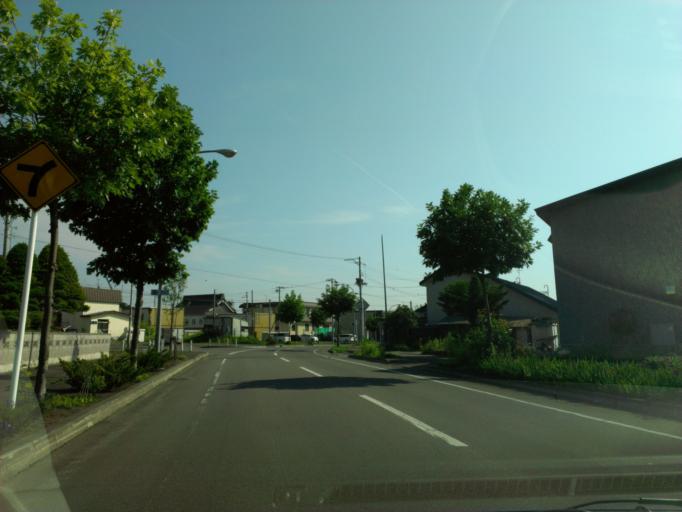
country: JP
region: Hokkaido
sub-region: Asahikawa-shi
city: Asahikawa
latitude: 43.5957
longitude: 142.4690
